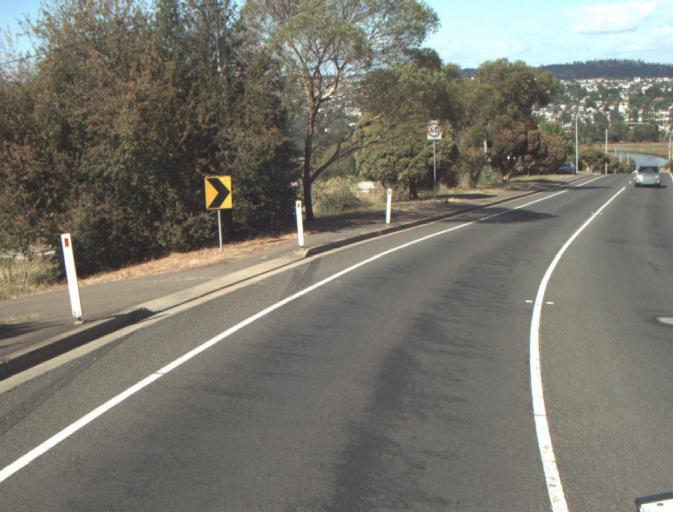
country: AU
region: Tasmania
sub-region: Launceston
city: Newstead
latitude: -41.4293
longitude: 147.1759
